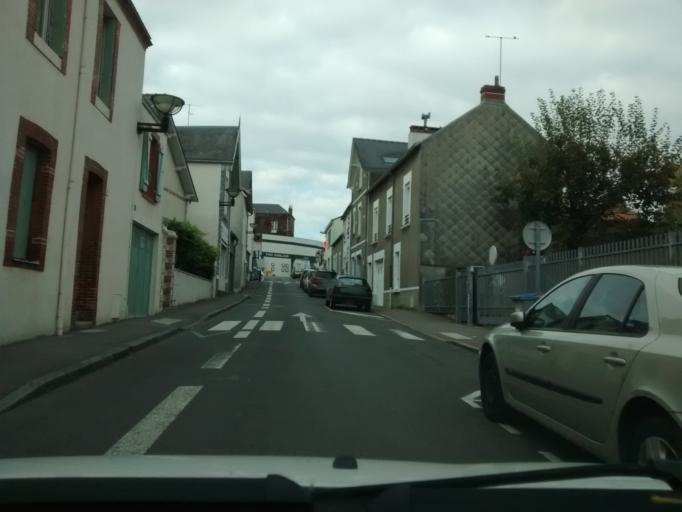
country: FR
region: Pays de la Loire
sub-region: Departement de la Loire-Atlantique
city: Coueron
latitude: 47.2100
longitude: -1.7277
